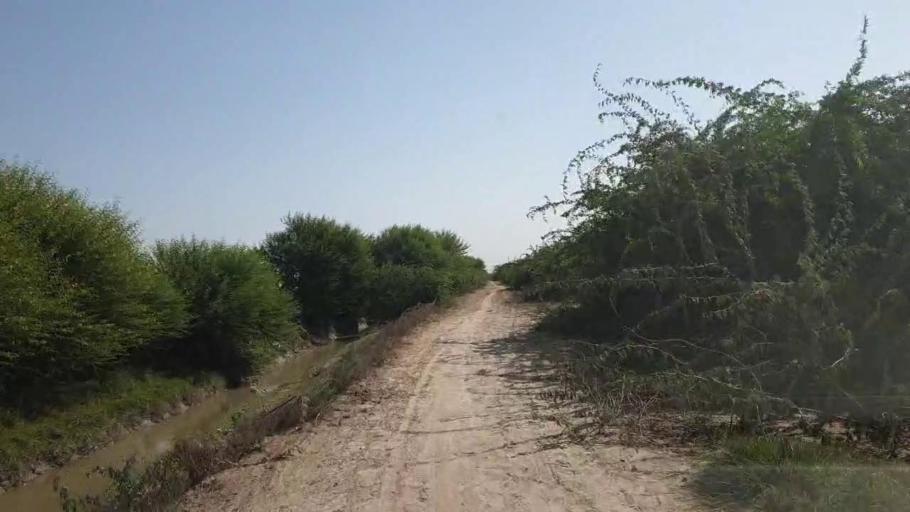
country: PK
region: Sindh
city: Kadhan
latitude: 24.5881
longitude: 69.0094
